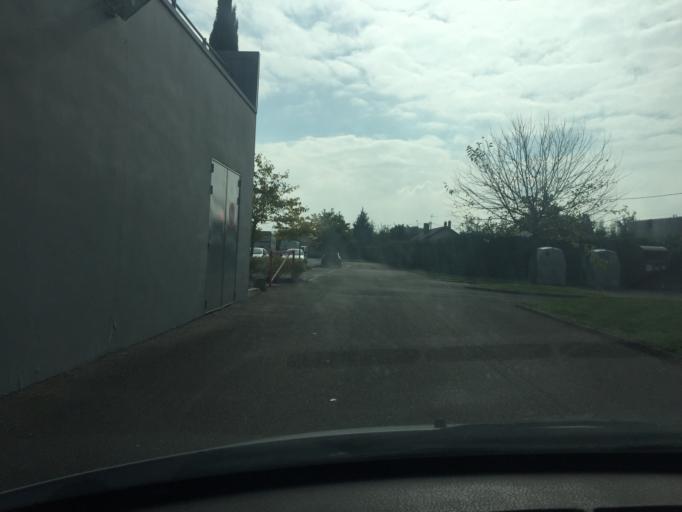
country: FR
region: Rhone-Alpes
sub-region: Departement de l'Ain
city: Saint-Maurice-de-Beynost
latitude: 45.8289
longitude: 4.9689
